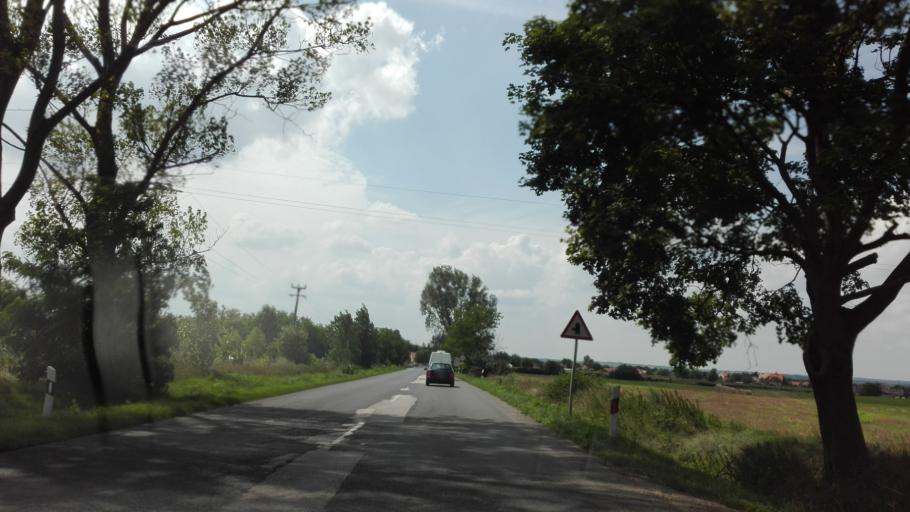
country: HU
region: Fejer
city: Cece
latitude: 46.7748
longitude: 18.6466
